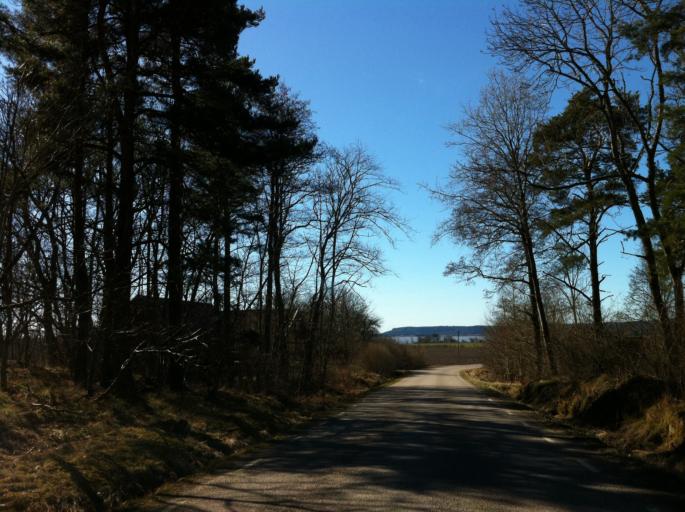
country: SE
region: Vaestra Goetaland
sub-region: Grastorps Kommun
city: Graestorp
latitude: 58.4333
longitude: 12.6080
